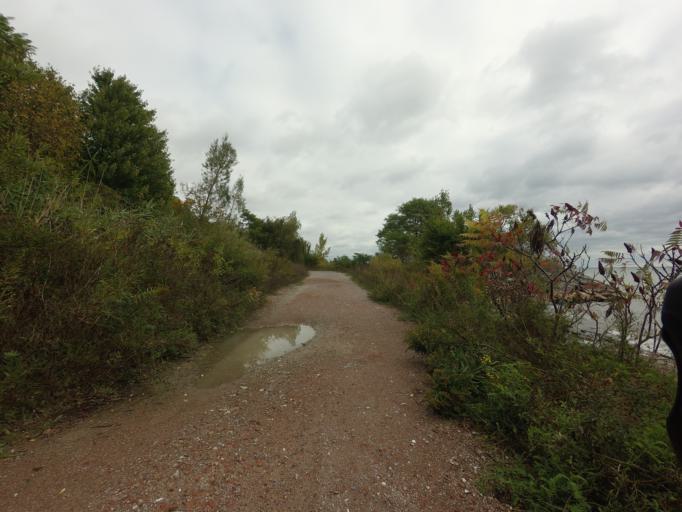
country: CA
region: Ontario
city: Scarborough
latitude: 43.7317
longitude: -79.2097
